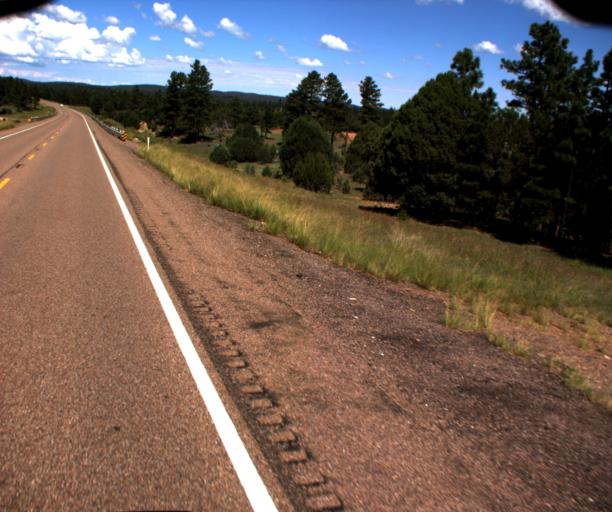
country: US
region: Arizona
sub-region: Navajo County
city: Linden
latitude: 34.3053
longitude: -110.2061
